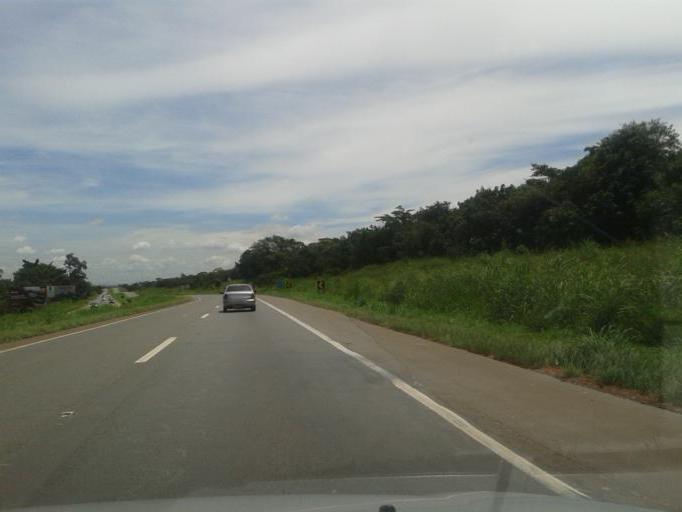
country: BR
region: Goias
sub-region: Hidrolandia
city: Hidrolandia
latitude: -16.9128
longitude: -49.2532
